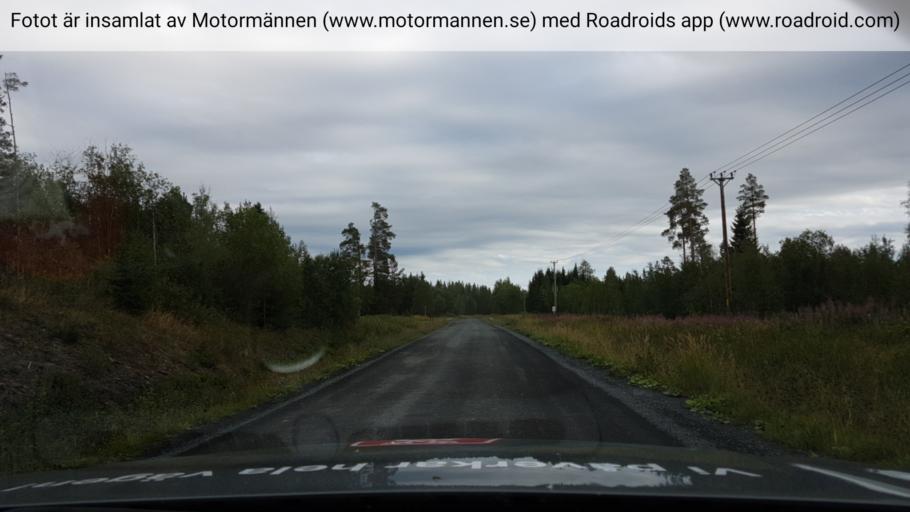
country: SE
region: Jaemtland
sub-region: Krokoms Kommun
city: Valla
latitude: 63.3484
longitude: 13.9959
